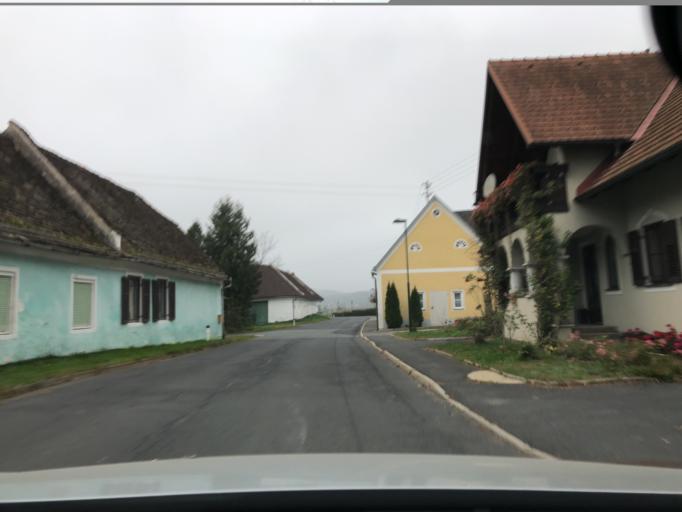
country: AT
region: Styria
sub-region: Politischer Bezirk Suedoststeiermark
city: Fehring
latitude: 46.9557
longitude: 16.0357
